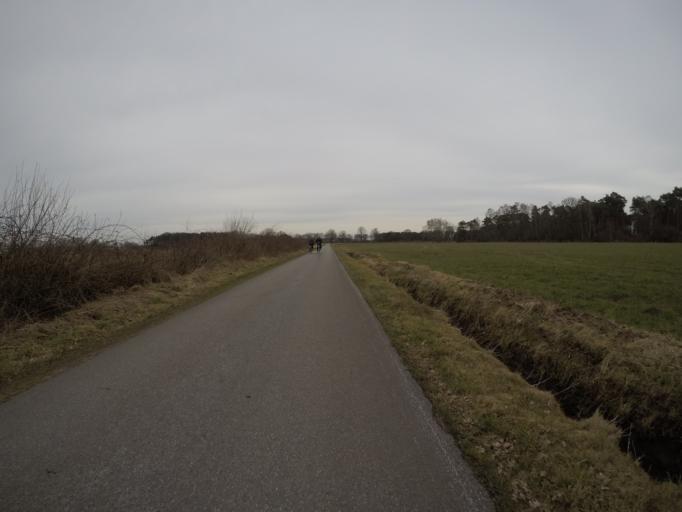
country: DE
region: North Rhine-Westphalia
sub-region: Regierungsbezirk Dusseldorf
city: Bocholt
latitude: 51.7963
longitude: 6.6327
